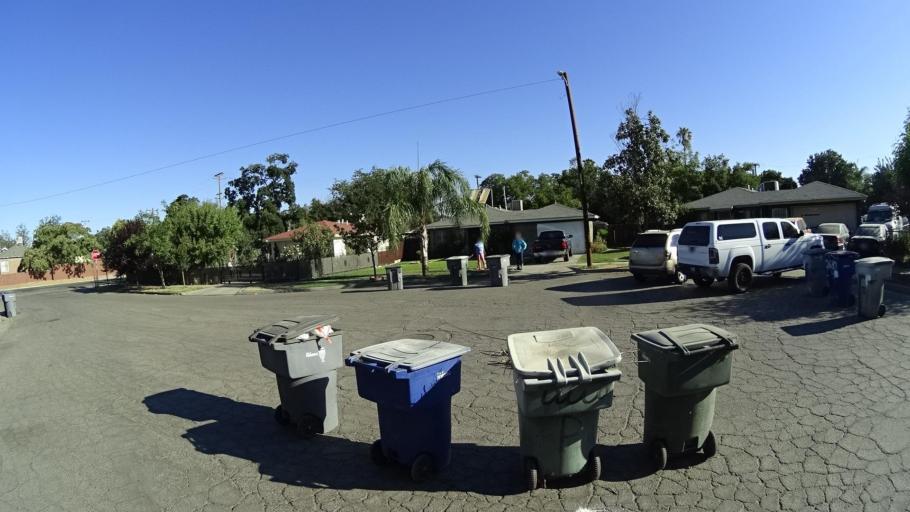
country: US
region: California
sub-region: Fresno County
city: Fresno
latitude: 36.7033
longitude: -119.7971
